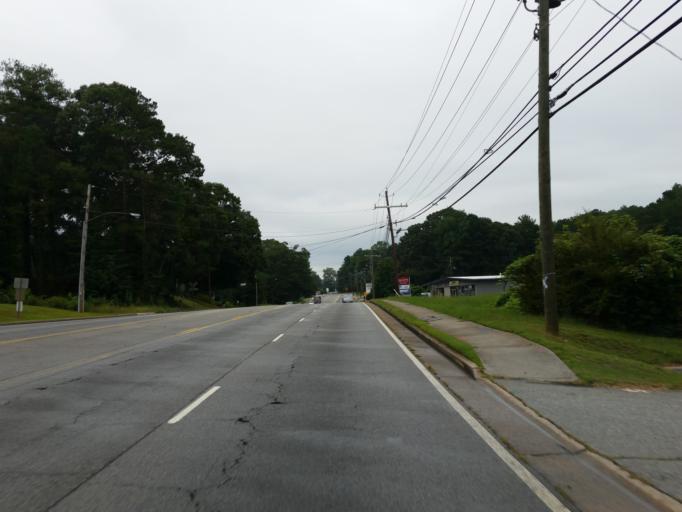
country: US
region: Georgia
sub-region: Cobb County
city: Mableton
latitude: 33.8174
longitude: -84.6064
